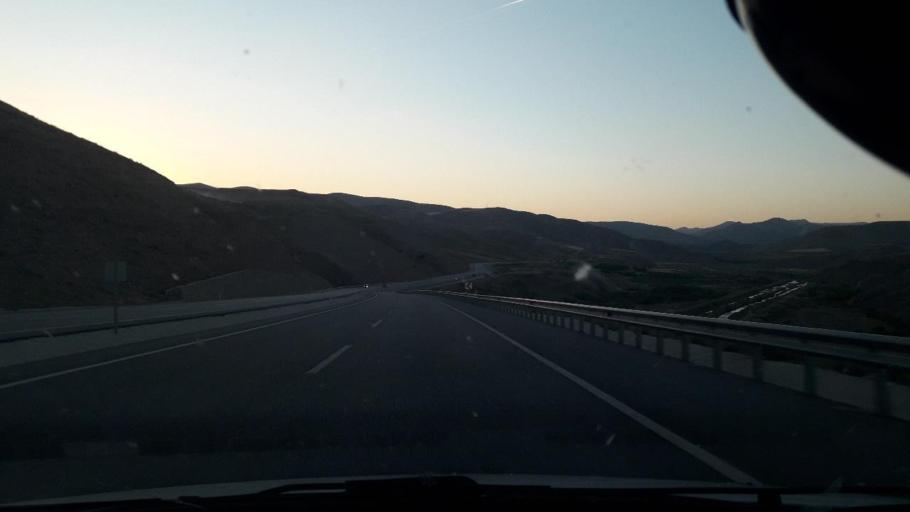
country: TR
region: Malatya
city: Yazihan
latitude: 38.6222
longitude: 38.1675
